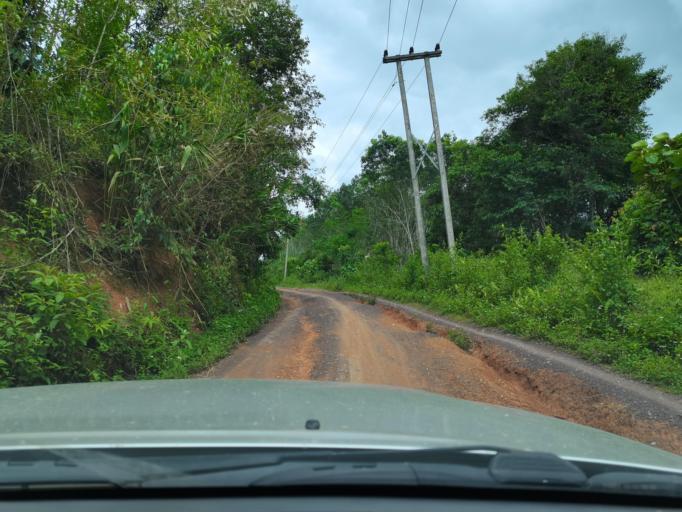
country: LA
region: Loungnamtha
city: Muang Long
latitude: 20.7006
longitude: 101.0221
